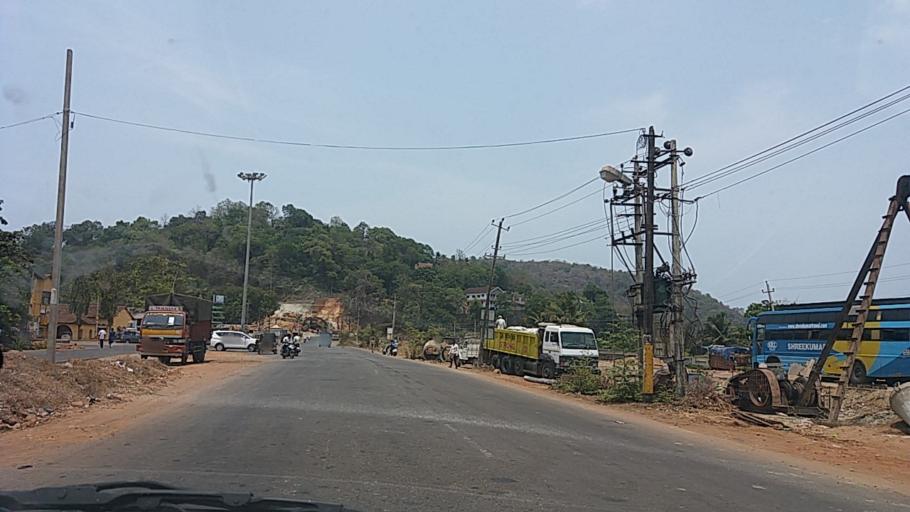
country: IN
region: Karnataka
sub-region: Uttar Kannada
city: Karwar
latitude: 14.8070
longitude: 74.1260
